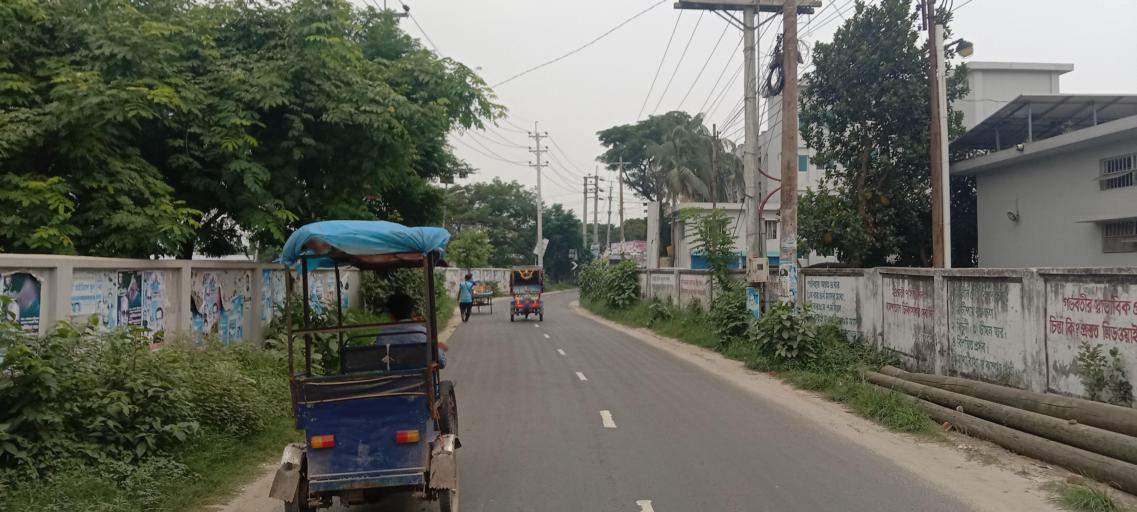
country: BD
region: Dhaka
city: Azimpur
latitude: 23.7073
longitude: 90.3477
